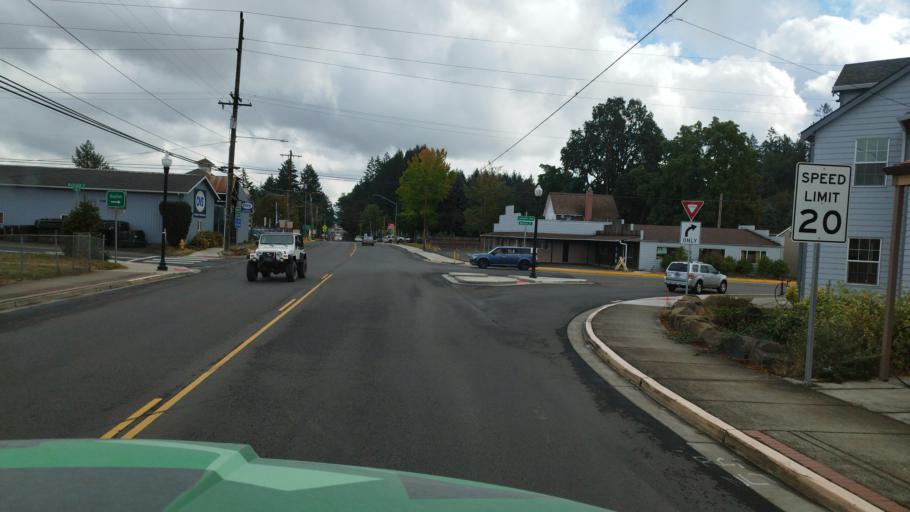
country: US
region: Oregon
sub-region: Yamhill County
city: Lafayette
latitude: 45.2436
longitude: -123.1126
